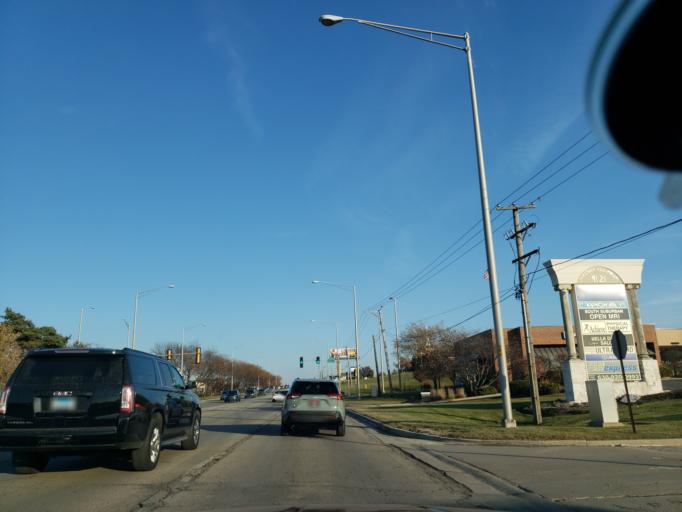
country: US
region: Illinois
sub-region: Cook County
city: Orland Hills
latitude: 41.6015
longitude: -87.8415
